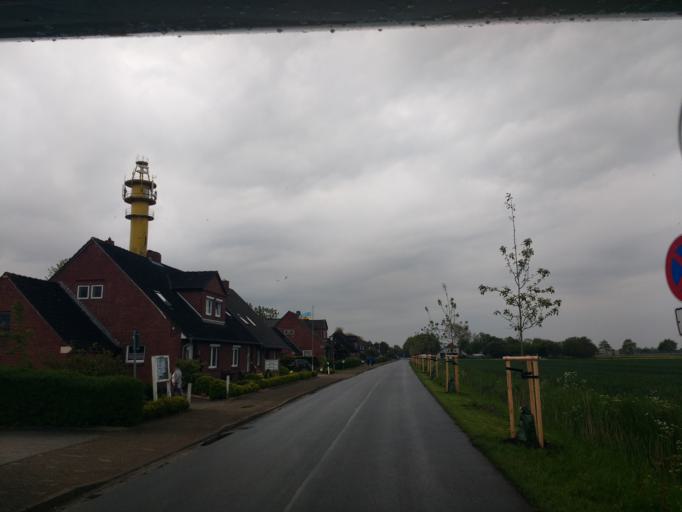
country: DE
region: Lower Saxony
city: Schillig
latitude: 53.7014
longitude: 8.0217
